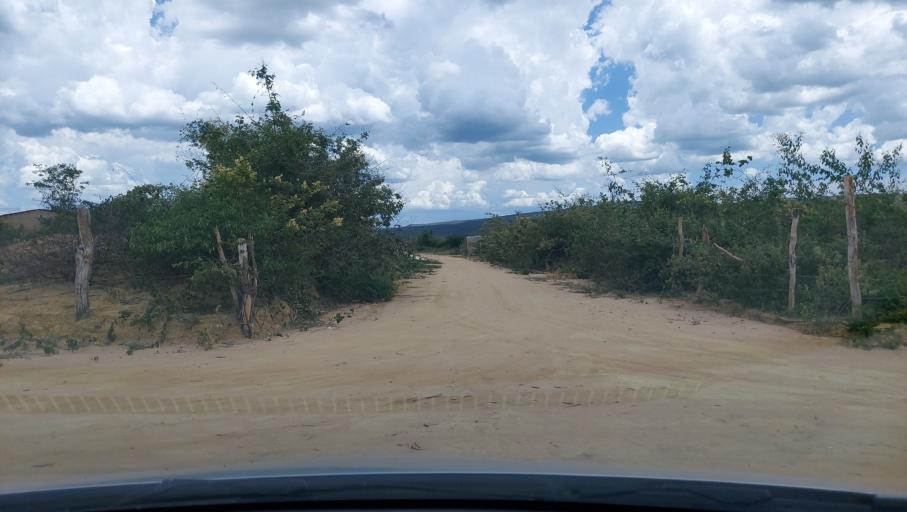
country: BR
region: Bahia
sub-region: Oliveira Dos Brejinhos
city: Beira Rio
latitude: -12.0065
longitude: -42.6345
